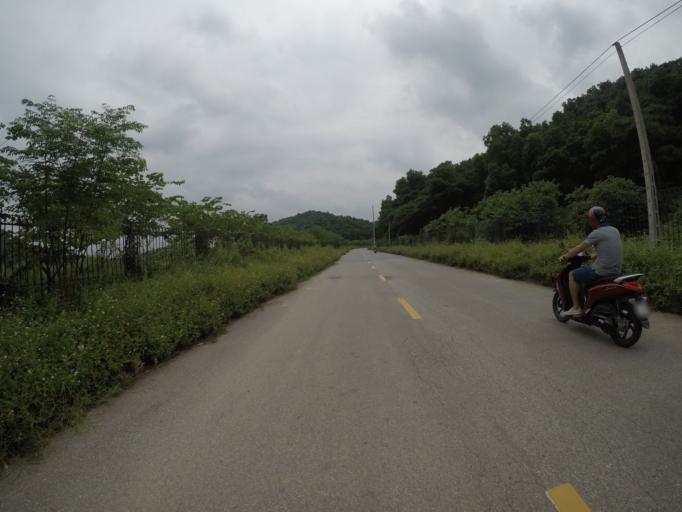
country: VN
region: Ha Noi
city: Soc Son
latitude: 21.2800
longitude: 105.8310
